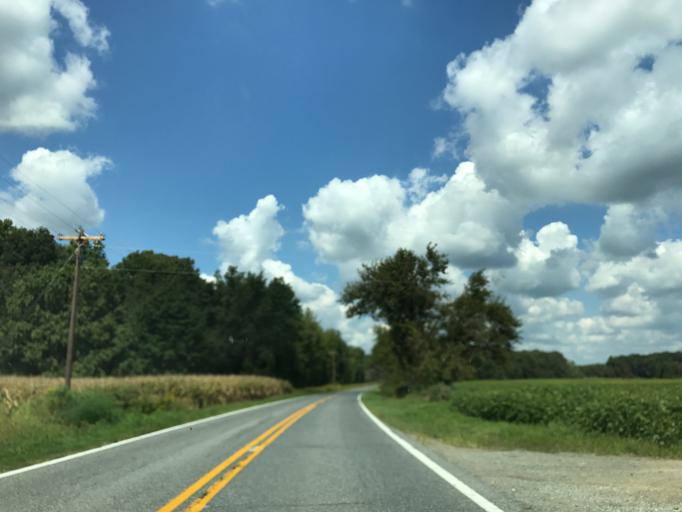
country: US
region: Maryland
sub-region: Caroline County
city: Ridgely
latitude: 39.0527
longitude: -75.9211
